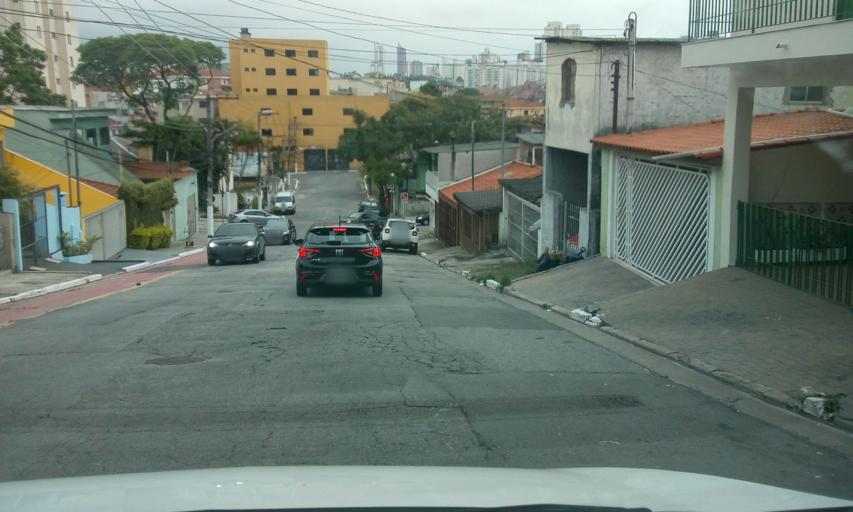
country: BR
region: Sao Paulo
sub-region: Sao Caetano Do Sul
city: Sao Caetano do Sul
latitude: -23.6185
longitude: -46.6073
